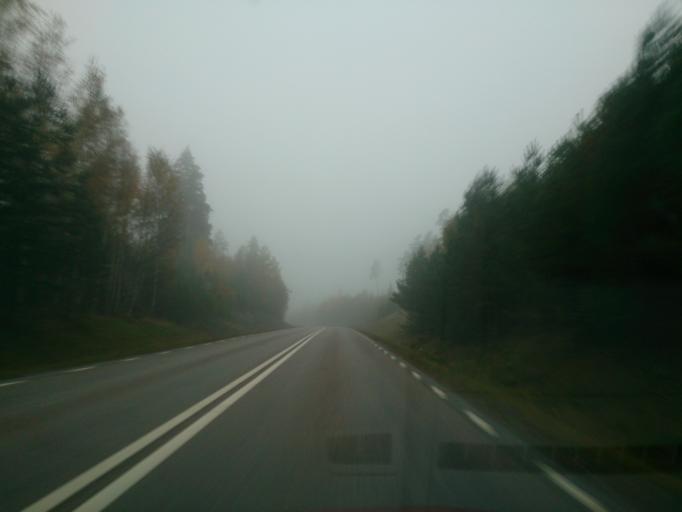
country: SE
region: OEstergoetland
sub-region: Atvidabergs Kommun
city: Atvidaberg
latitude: 58.1728
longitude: 15.9674
